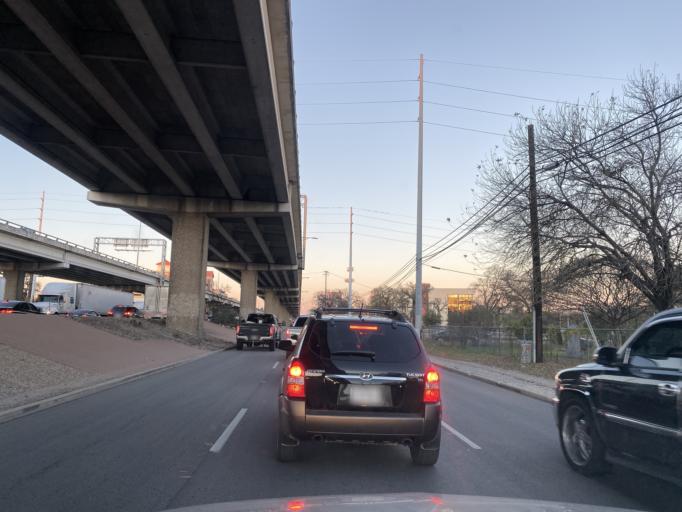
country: US
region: Texas
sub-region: Travis County
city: Austin
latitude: 30.2857
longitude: -97.7252
